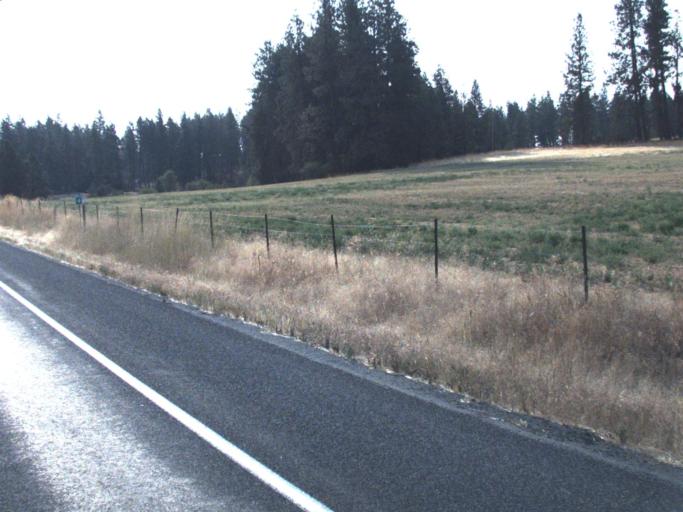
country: US
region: Idaho
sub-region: Benewah County
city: Plummer
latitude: 47.4431
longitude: -117.0696
